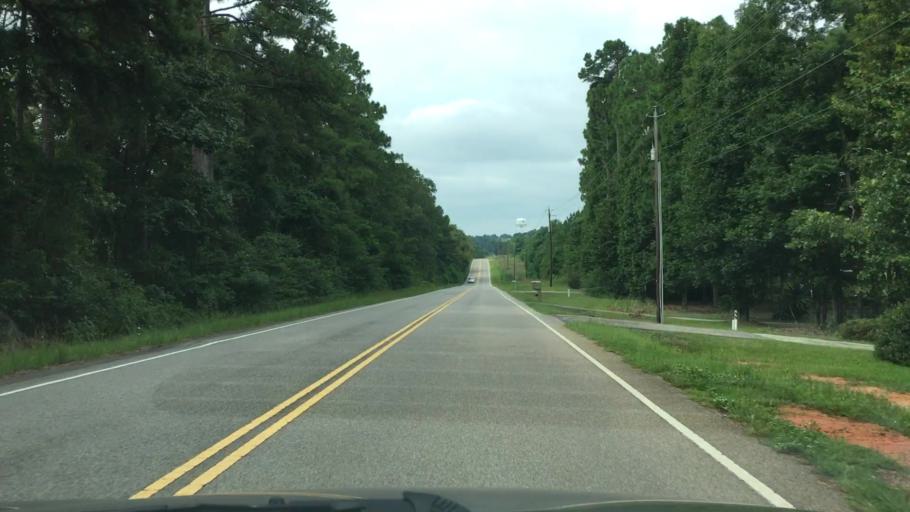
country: US
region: South Carolina
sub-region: Aiken County
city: Belvedere
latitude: 33.5583
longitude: -81.9454
